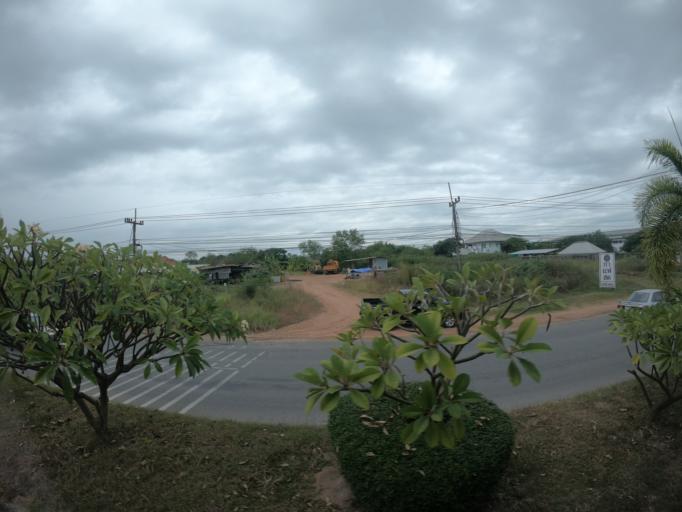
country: TH
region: Maha Sarakham
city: Maha Sarakham
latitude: 16.1712
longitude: 103.2928
